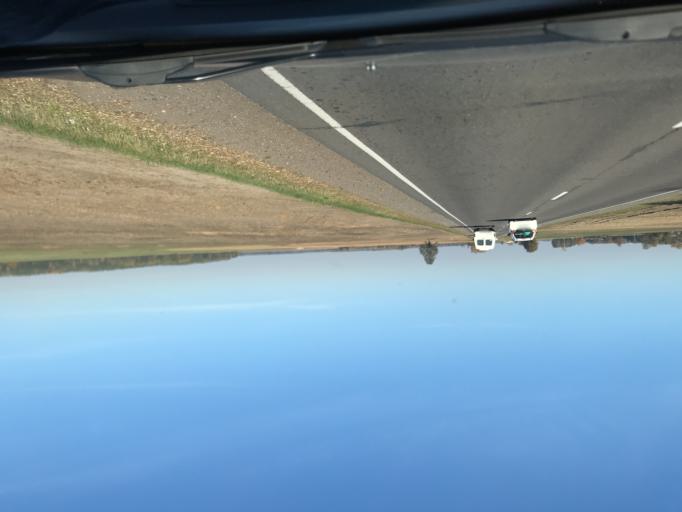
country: BY
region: Gomel
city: Parychy
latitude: 52.6462
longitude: 29.3732
